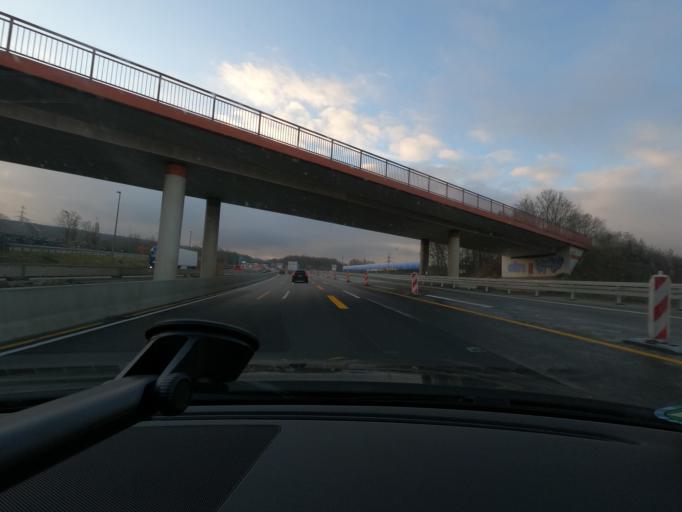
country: DE
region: Hesse
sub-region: Regierungsbezirk Kassel
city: Lohfelden
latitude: 51.2657
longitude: 9.5164
